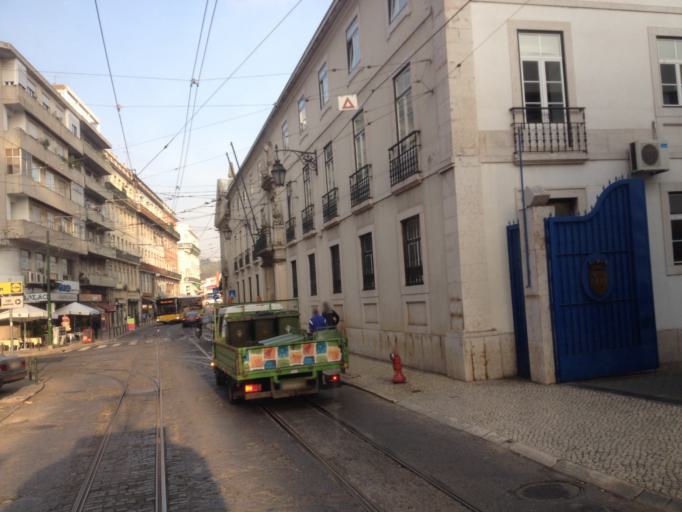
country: PT
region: Setubal
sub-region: Almada
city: Pragal
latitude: 38.7042
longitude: -9.1786
